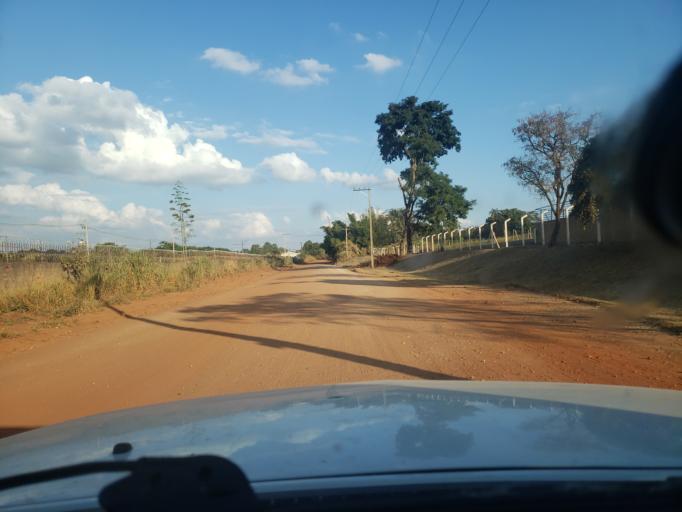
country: BR
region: Sao Paulo
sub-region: Mogi-Mirim
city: Mogi Mirim
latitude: -22.4550
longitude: -46.9427
